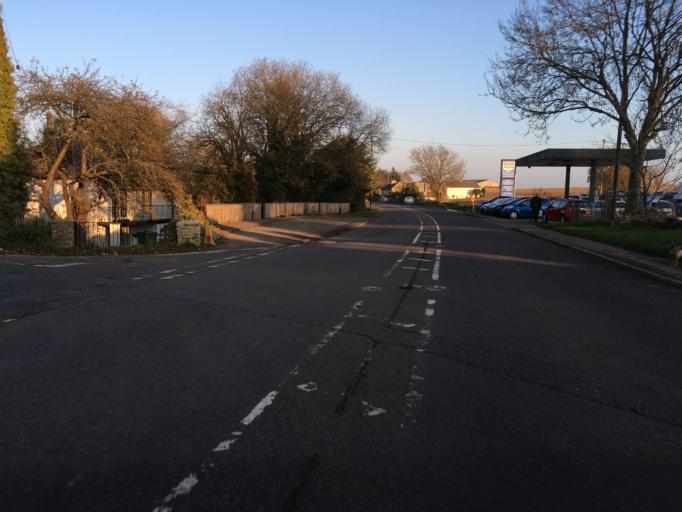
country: GB
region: England
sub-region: Wiltshire
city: Colerne
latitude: 51.4670
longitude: -2.2777
